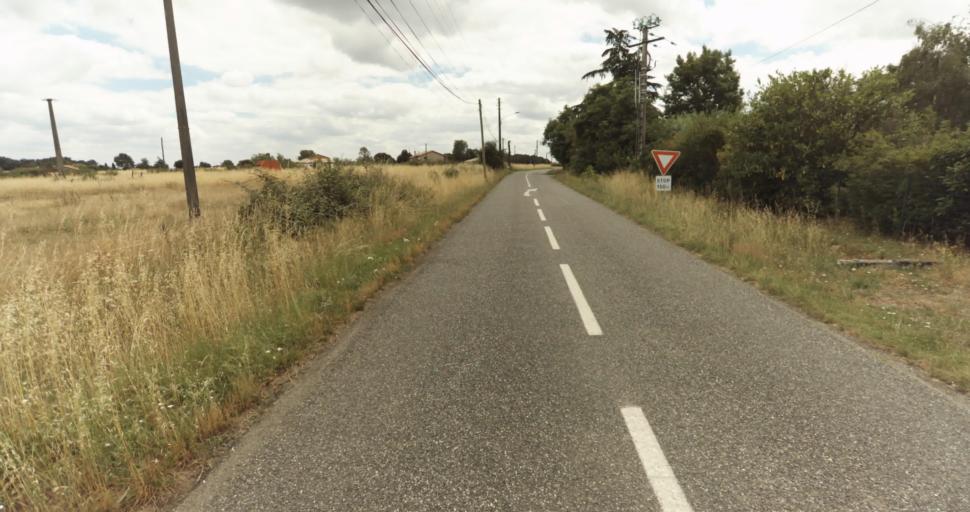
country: FR
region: Midi-Pyrenees
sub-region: Departement de la Haute-Garonne
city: Fontenilles
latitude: 43.5504
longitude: 1.2072
